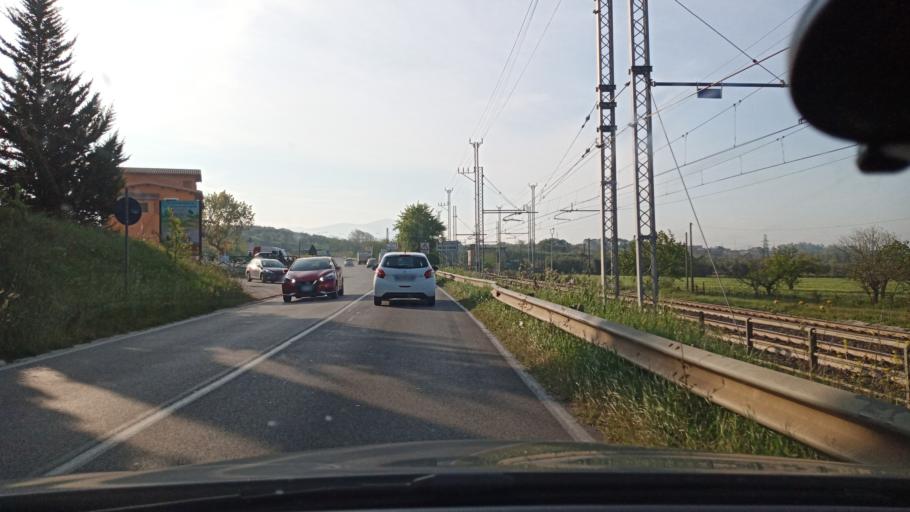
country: IT
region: Latium
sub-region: Citta metropolitana di Roma Capitale
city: Fiano Romano
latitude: 42.1644
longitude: 12.6440
